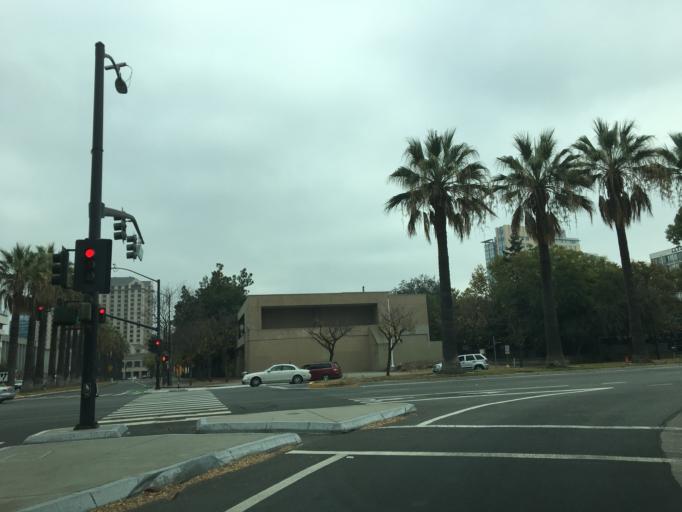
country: US
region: California
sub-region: Santa Clara County
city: San Jose
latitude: 37.3306
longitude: -121.8928
